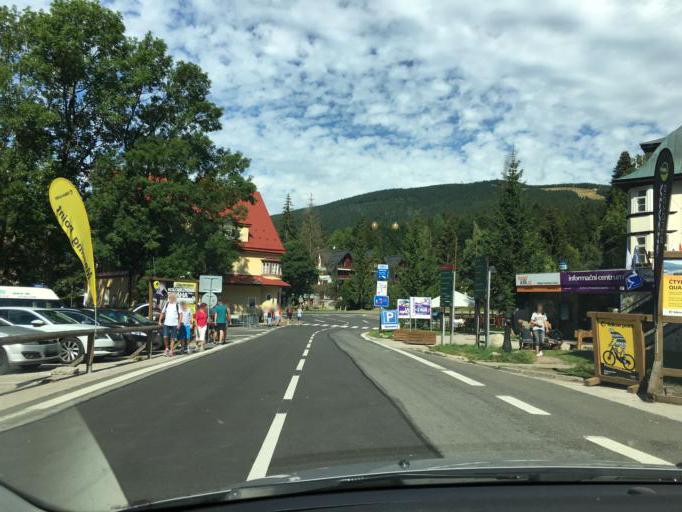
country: CZ
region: Kralovehradecky
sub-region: Okres Trutnov
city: Spindleruv Mlyn
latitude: 50.7252
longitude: 15.6075
